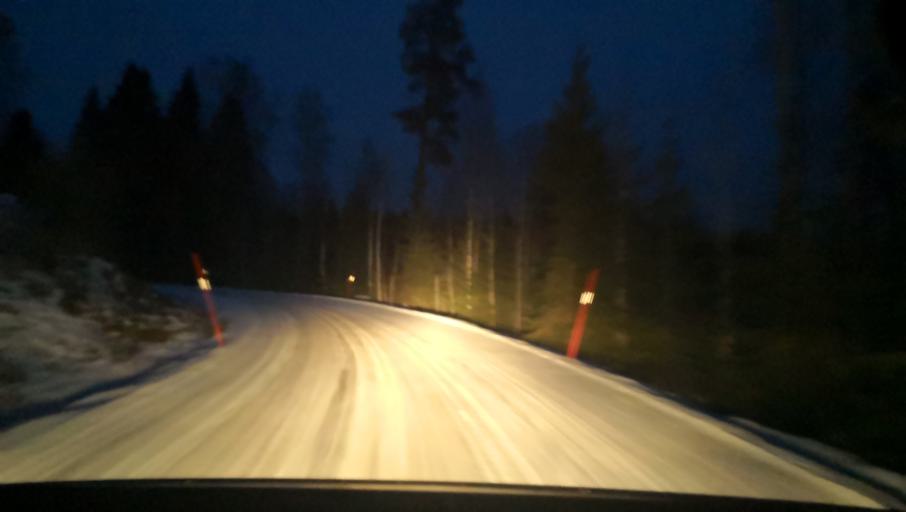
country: SE
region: Uppsala
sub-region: Heby Kommun
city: Tarnsjo
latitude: 60.2569
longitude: 16.7735
